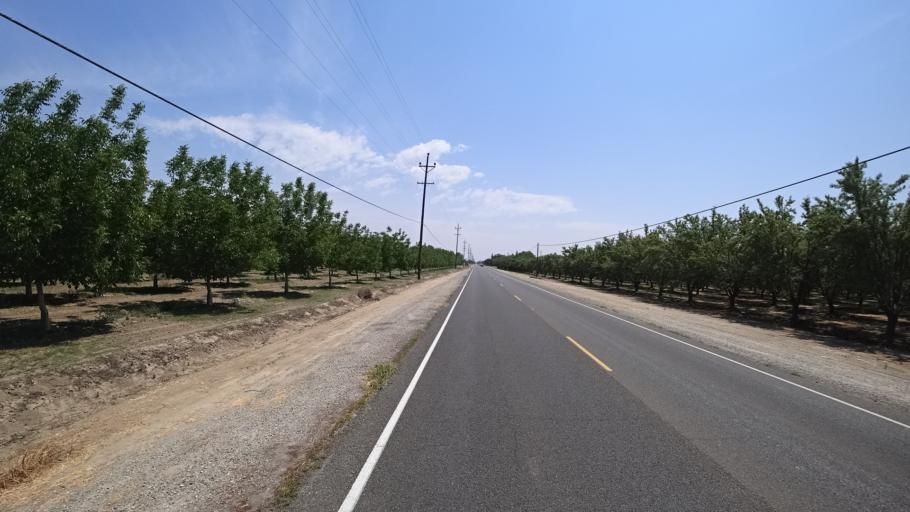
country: US
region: California
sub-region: Kings County
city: Armona
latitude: 36.3136
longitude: -119.7305
